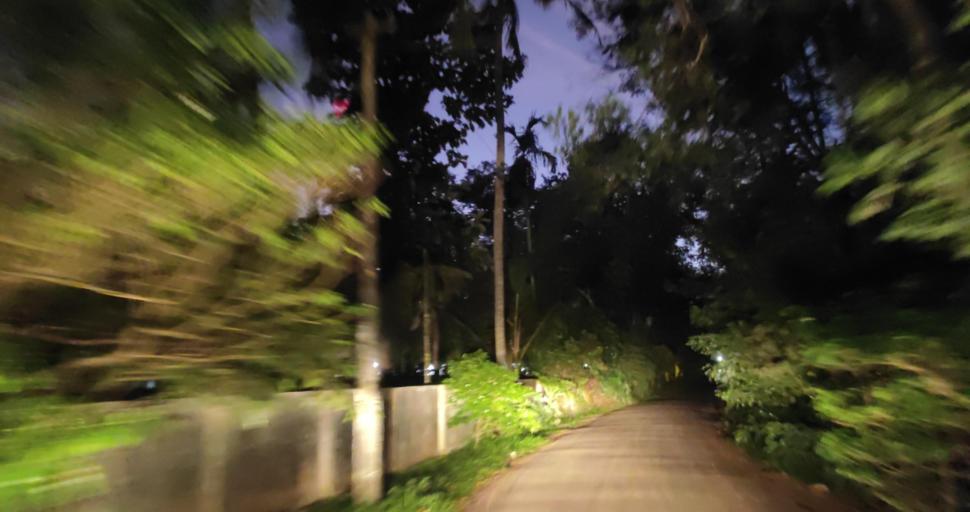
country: IN
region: Kerala
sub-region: Alappuzha
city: Shertallai
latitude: 9.6237
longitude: 76.3481
